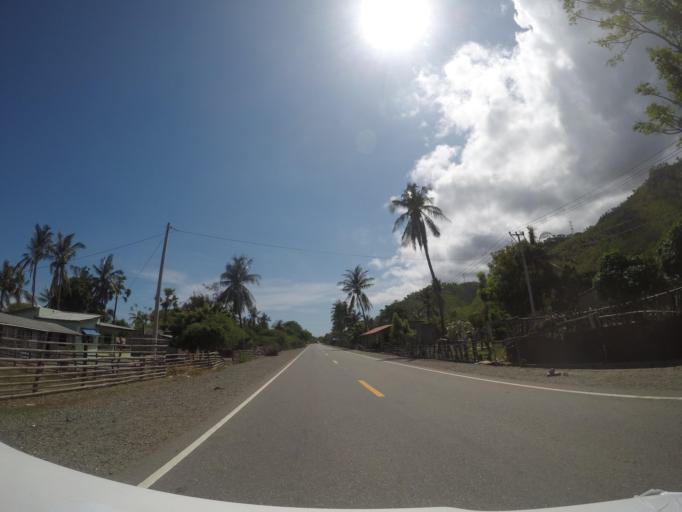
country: ID
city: Metinaro
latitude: -8.4767
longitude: 125.8569
